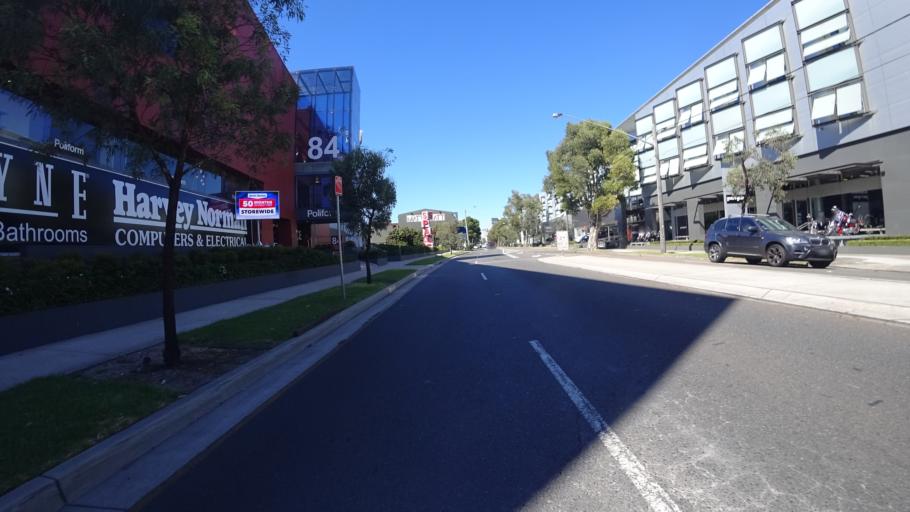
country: AU
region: New South Wales
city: Alexandria
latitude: -33.9175
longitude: 151.1939
